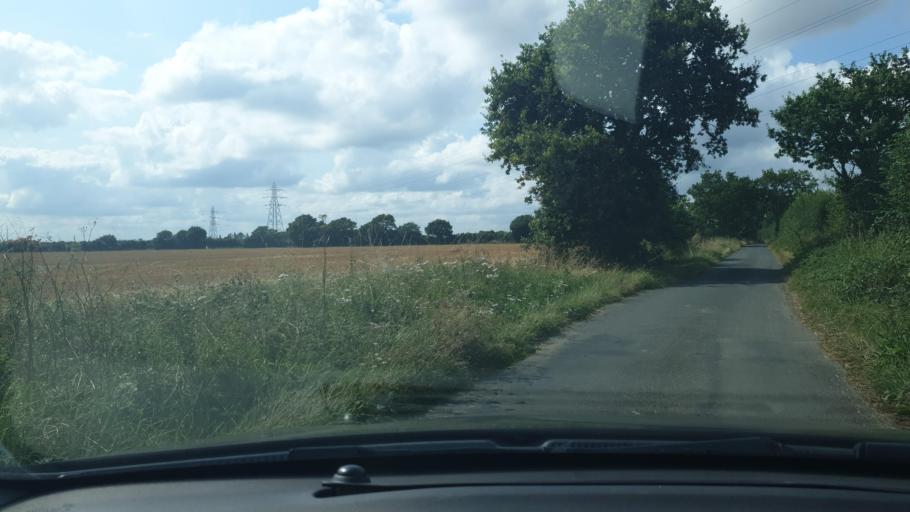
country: GB
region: England
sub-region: Essex
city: Manningtree
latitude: 51.9209
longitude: 1.0247
